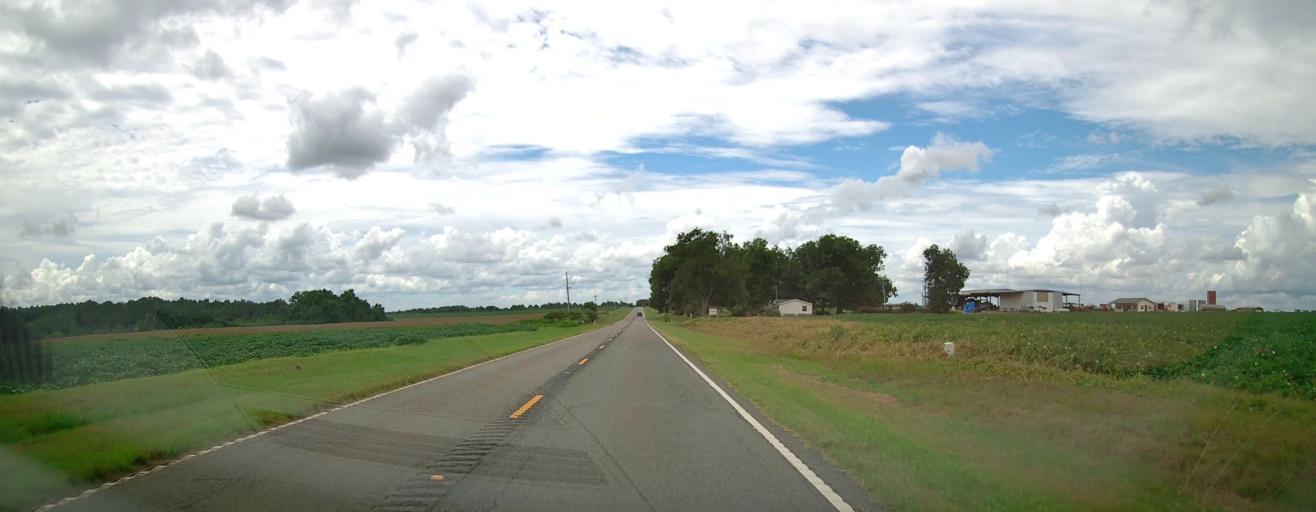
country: US
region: Georgia
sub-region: Dooly County
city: Unadilla
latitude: 32.2589
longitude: -83.7858
